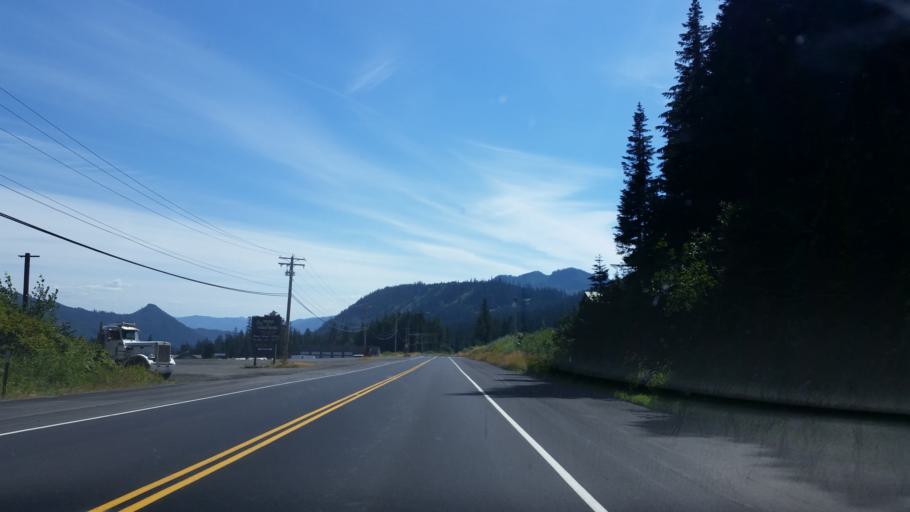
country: US
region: Washington
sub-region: King County
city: Tanner
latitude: 47.4122
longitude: -121.4130
